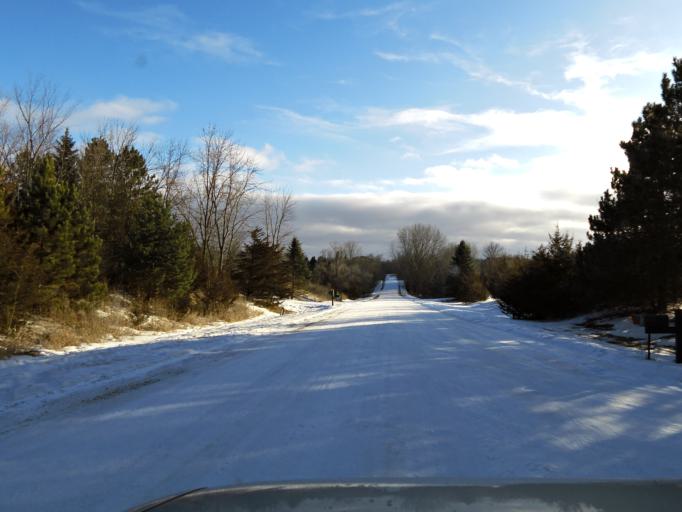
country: US
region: Wisconsin
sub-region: Pierce County
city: Prescott
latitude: 44.7966
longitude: -92.8244
